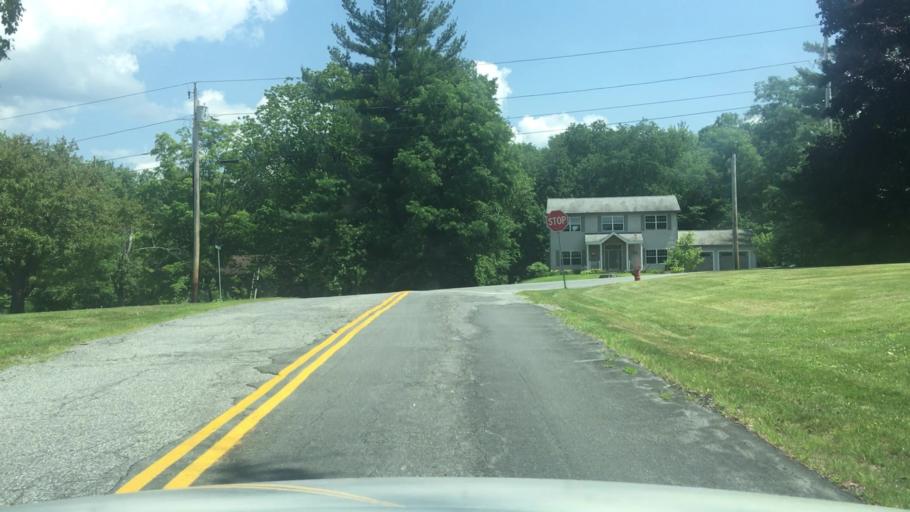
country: US
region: New Hampshire
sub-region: Grafton County
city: Lebanon
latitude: 43.6350
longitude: -72.2224
